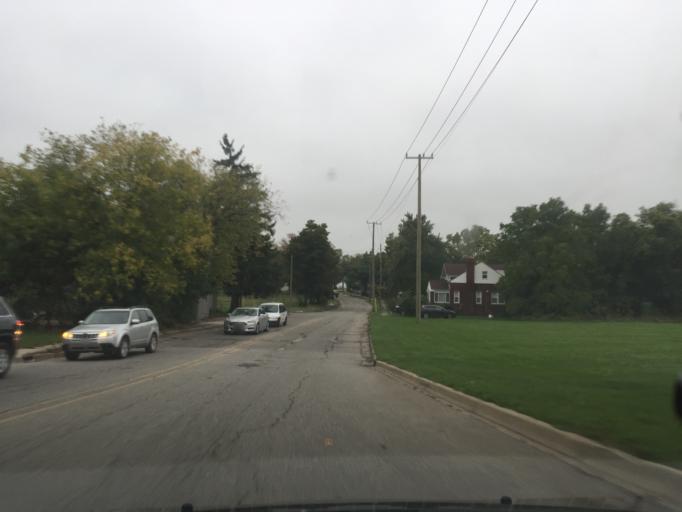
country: US
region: Michigan
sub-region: Oakland County
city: Pontiac
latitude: 42.6406
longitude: -83.2822
